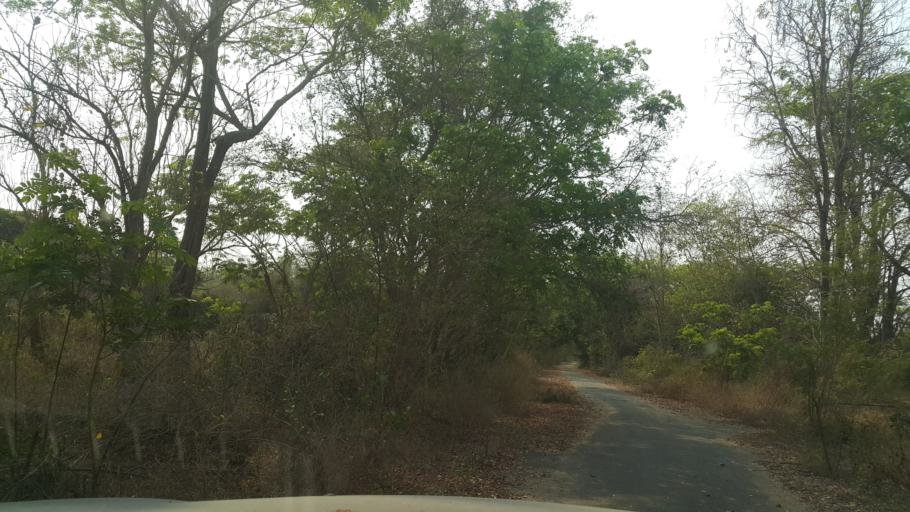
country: TH
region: Chiang Mai
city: San Kamphaeng
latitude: 18.7636
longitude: 99.1117
